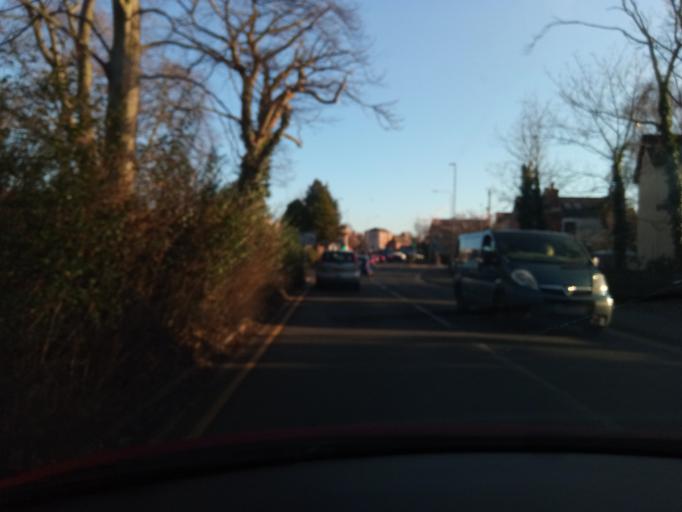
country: GB
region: England
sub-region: Leicestershire
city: Loughborough
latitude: 52.7688
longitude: -1.2095
